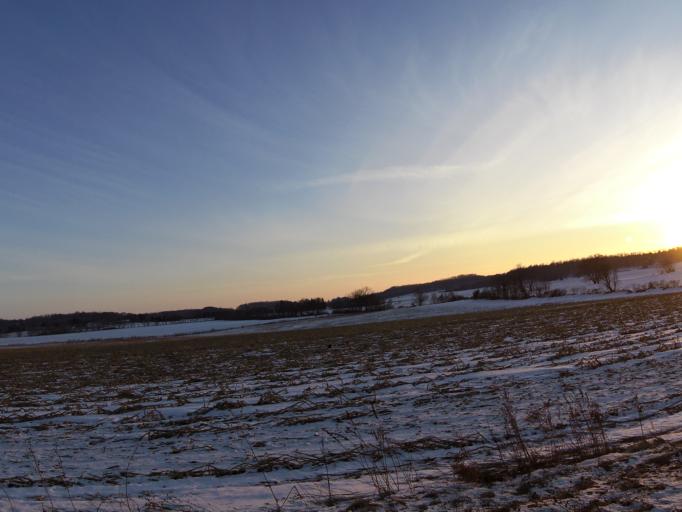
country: US
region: Wisconsin
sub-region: Pierce County
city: River Falls
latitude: 44.8768
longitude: -92.6733
